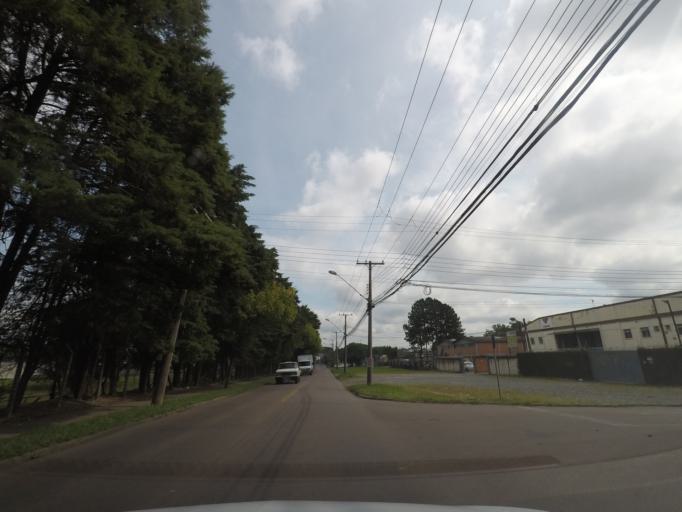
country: BR
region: Parana
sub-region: Curitiba
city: Curitiba
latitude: -25.4945
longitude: -49.3277
